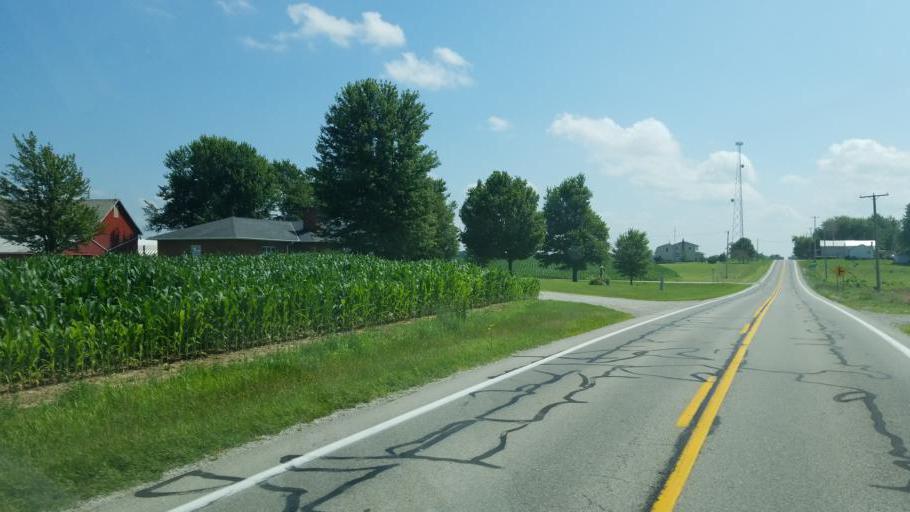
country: US
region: Ohio
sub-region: Huron County
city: Bellevue
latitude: 41.1545
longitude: -82.8458
